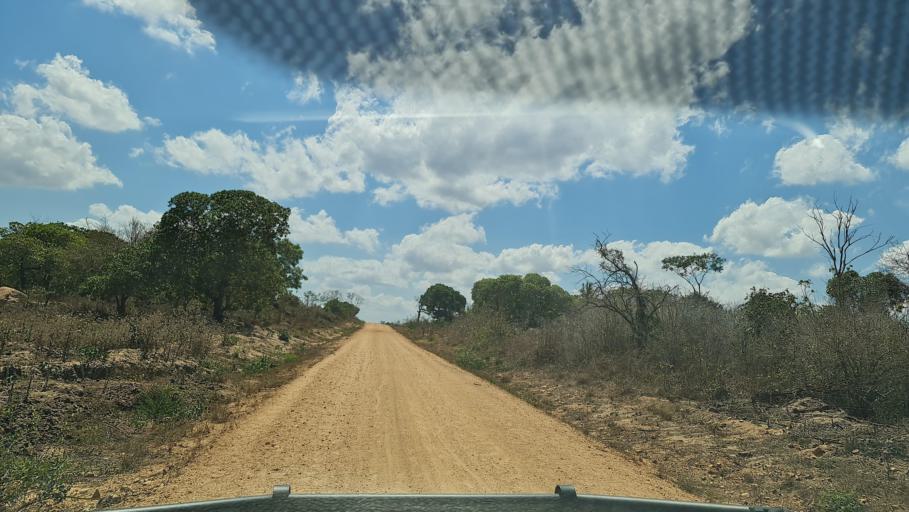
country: MZ
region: Nampula
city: Nacala
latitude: -14.1765
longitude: 40.2287
